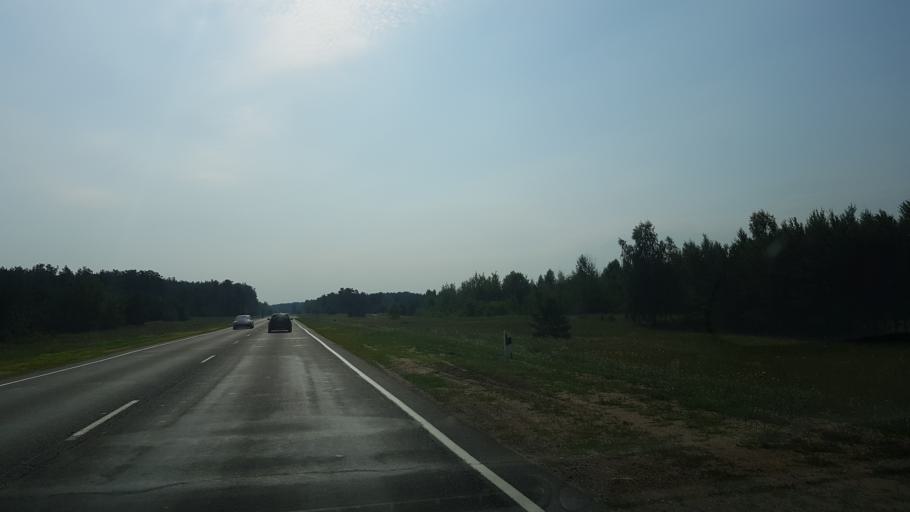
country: BY
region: Mogilev
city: Babruysk
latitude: 53.1663
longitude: 29.2841
